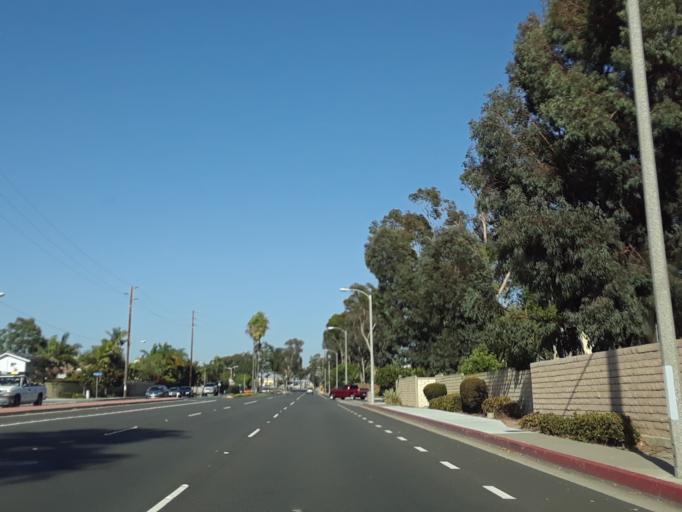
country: US
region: California
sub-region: Orange County
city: Huntington Beach
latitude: 33.6756
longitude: -118.0098
